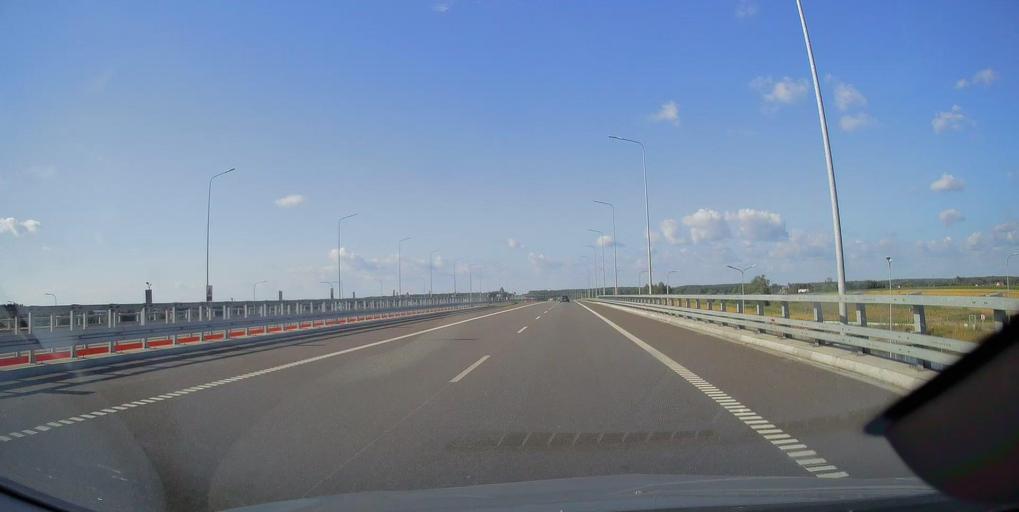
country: PL
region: Masovian Voivodeship
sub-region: Powiat radomski
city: Zakrzew
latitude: 51.4188
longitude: 21.0308
